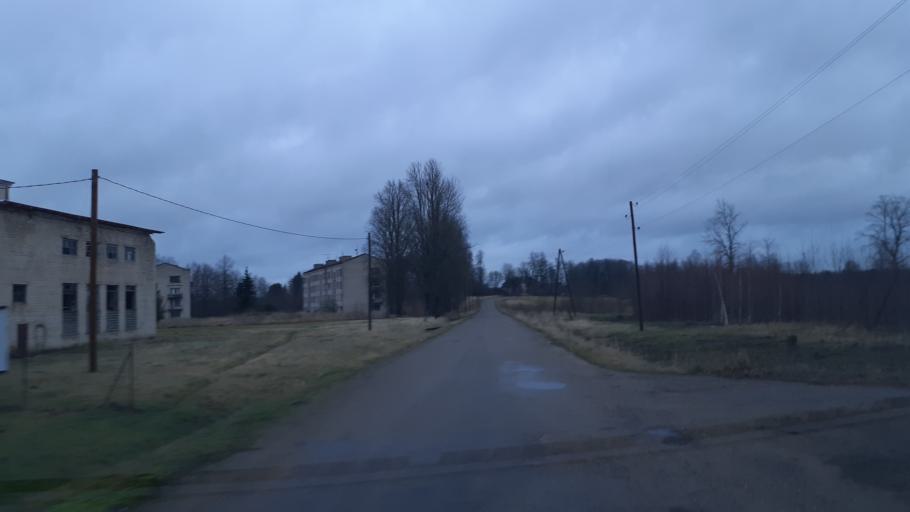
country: LV
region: Kuldigas Rajons
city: Kuldiga
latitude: 57.0392
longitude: 22.1271
